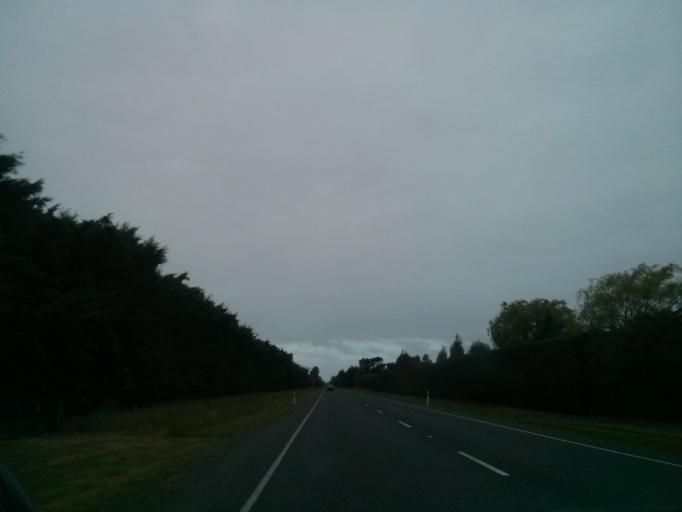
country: NZ
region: Canterbury
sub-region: Waimakariri District
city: Kaiapoi
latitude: -43.3810
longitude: 172.5410
